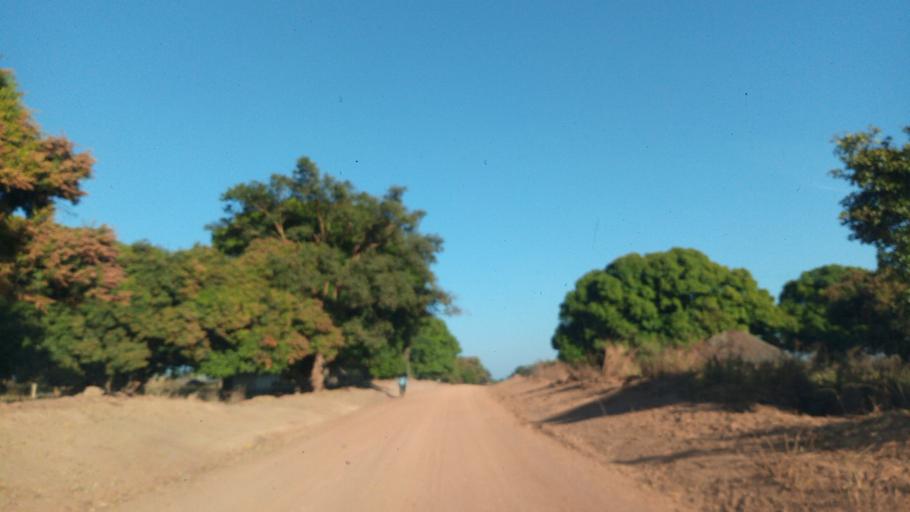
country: ZM
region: Luapula
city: Mwense
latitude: -10.4454
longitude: 28.5750
